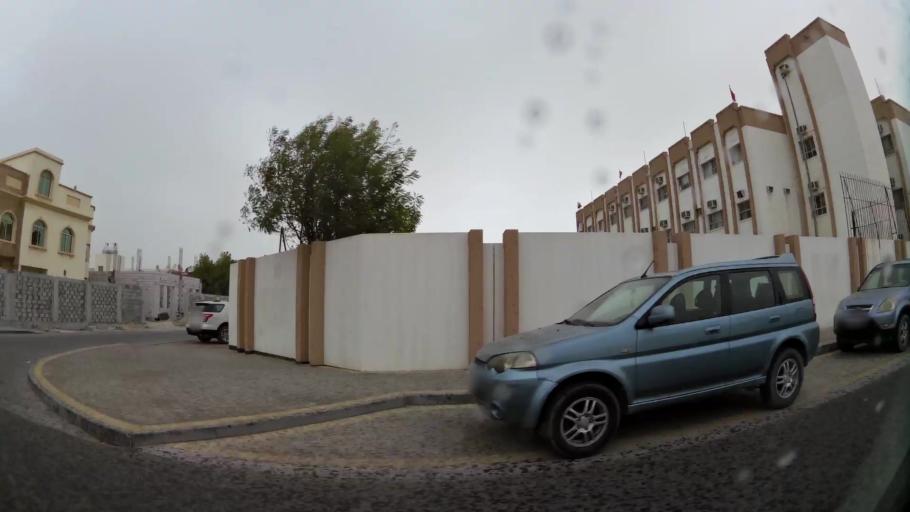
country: BH
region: Northern
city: Madinat `Isa
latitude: 26.1593
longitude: 50.5671
